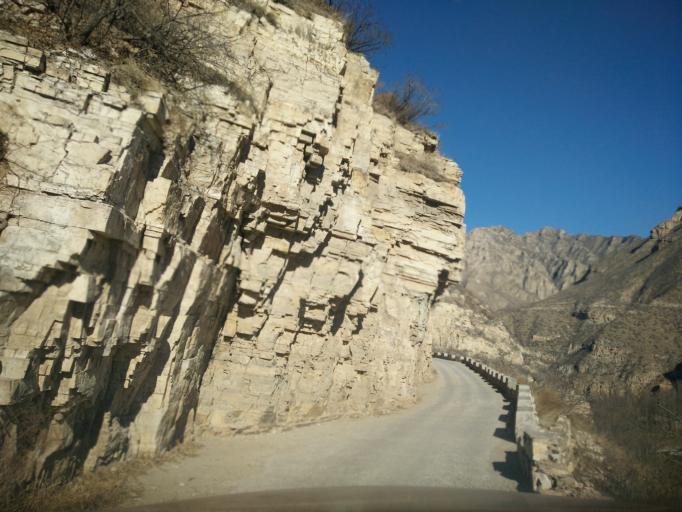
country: CN
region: Beijing
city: Zhaitang
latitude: 40.1555
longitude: 115.6783
